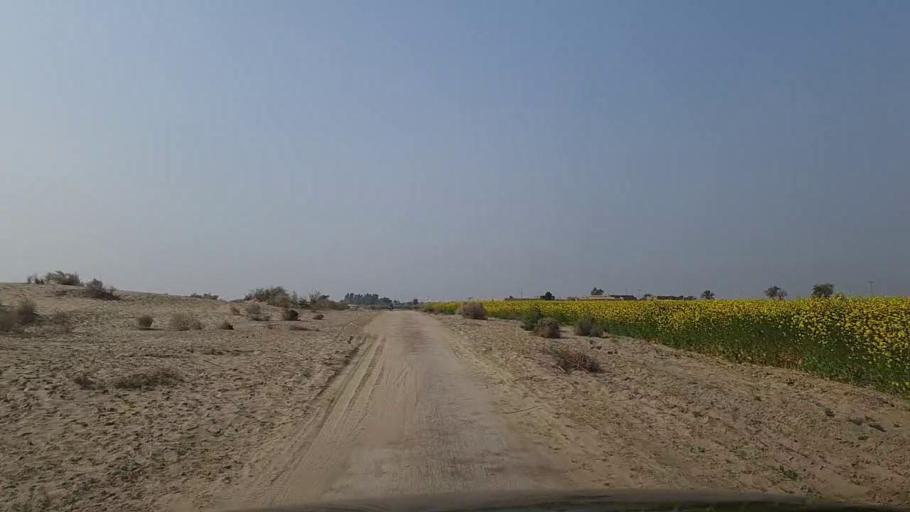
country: PK
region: Sindh
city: Daur
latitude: 26.3859
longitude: 68.4164
